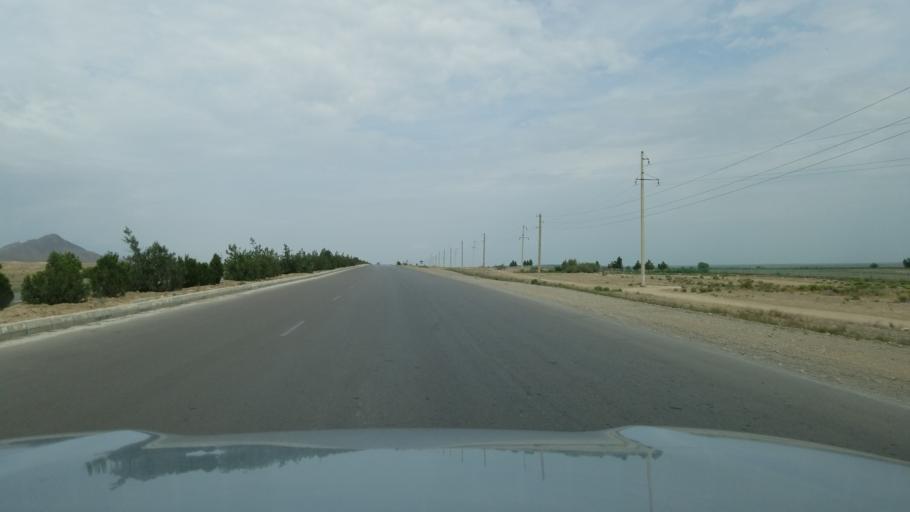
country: TM
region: Ahal
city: Baharly
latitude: 38.2272
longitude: 57.7922
